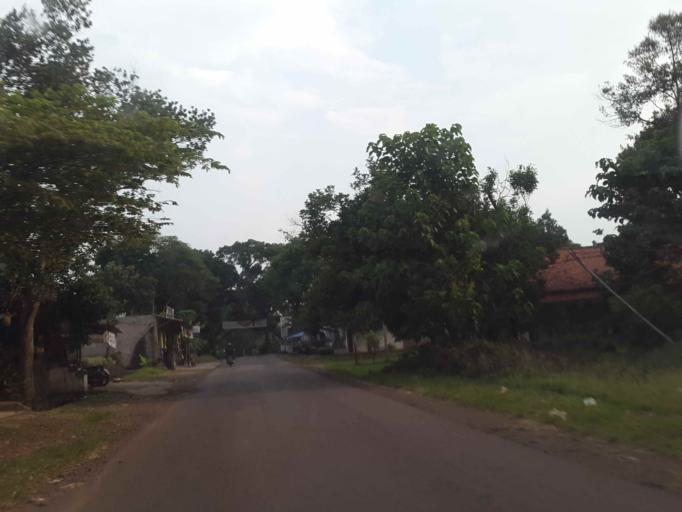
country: ID
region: West Java
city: Ciranjang-hilir
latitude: -6.7535
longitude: 107.1976
